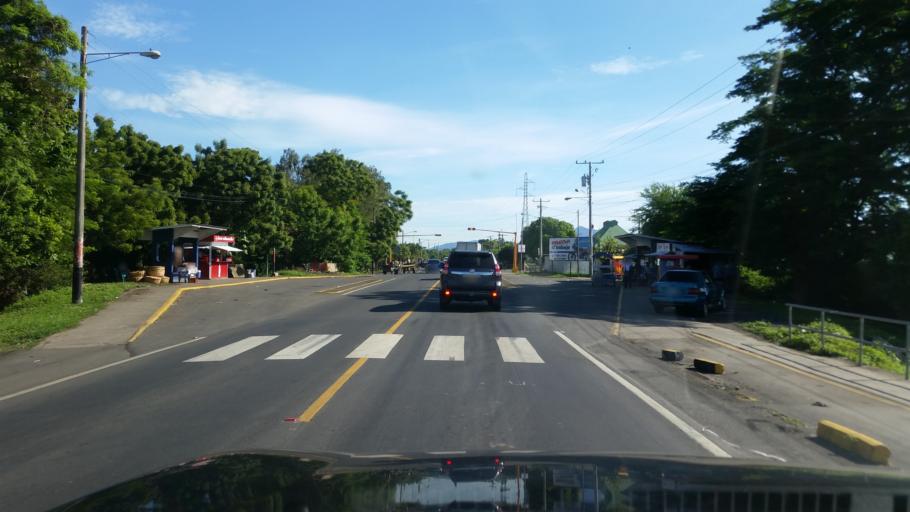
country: NI
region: Leon
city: Leon
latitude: 12.4420
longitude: -86.8632
